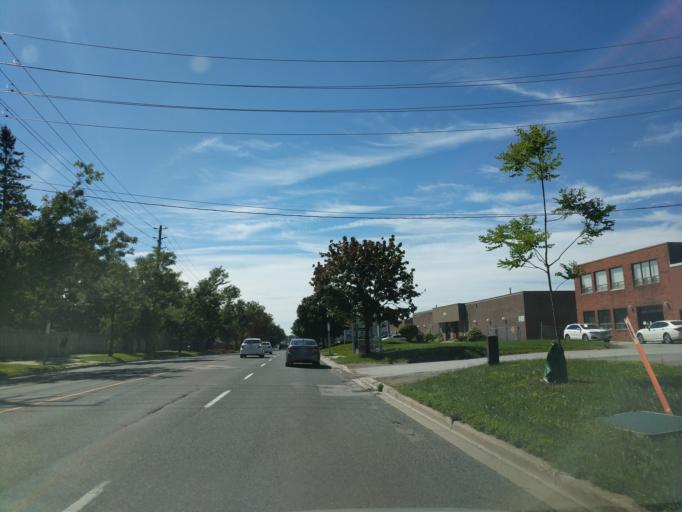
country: CA
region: Ontario
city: Scarborough
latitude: 43.8119
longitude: -79.2911
